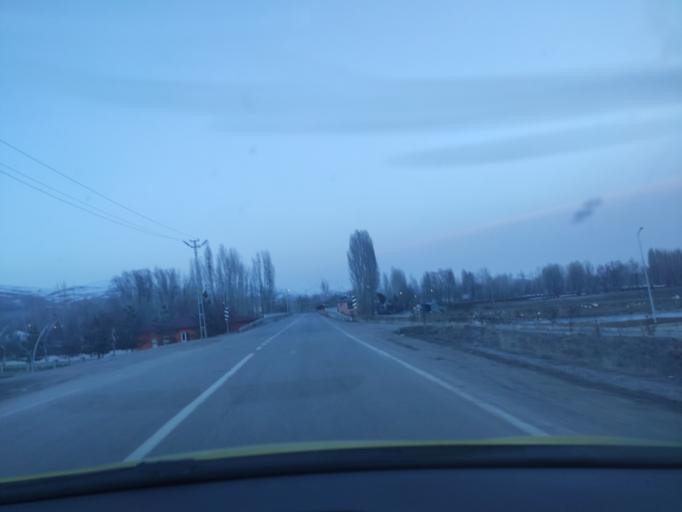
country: TR
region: Bayburt
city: Aydintepe
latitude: 40.3638
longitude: 40.1068
